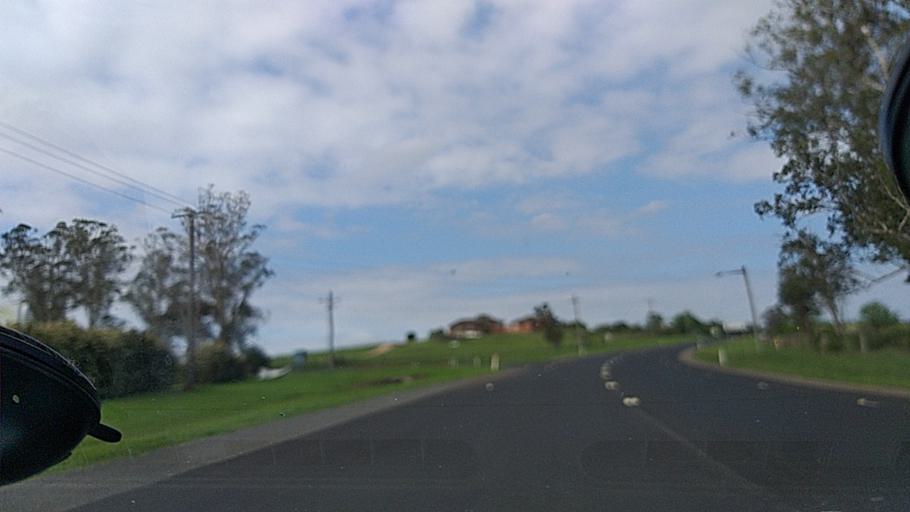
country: AU
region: New South Wales
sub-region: Campbelltown Municipality
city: Glen Alpine
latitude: -34.1089
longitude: 150.7483
